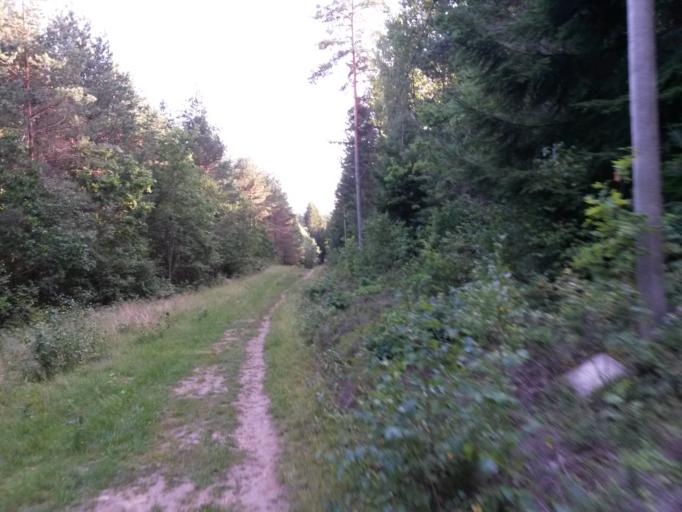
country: SE
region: Vaestra Goetaland
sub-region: Vargarda Kommun
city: Vargarda
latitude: 58.0372
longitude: 12.8401
